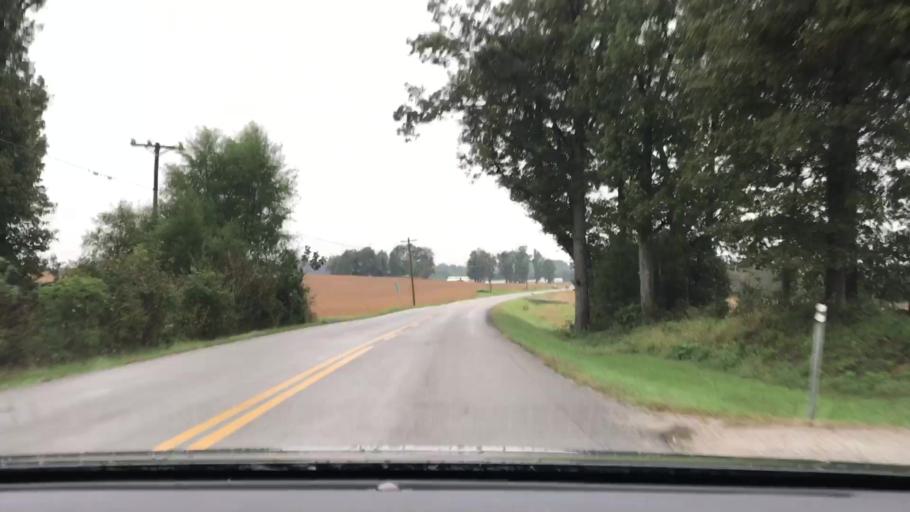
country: US
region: Kentucky
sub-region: McLean County
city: Calhoun
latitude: 37.4317
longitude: -87.2505
